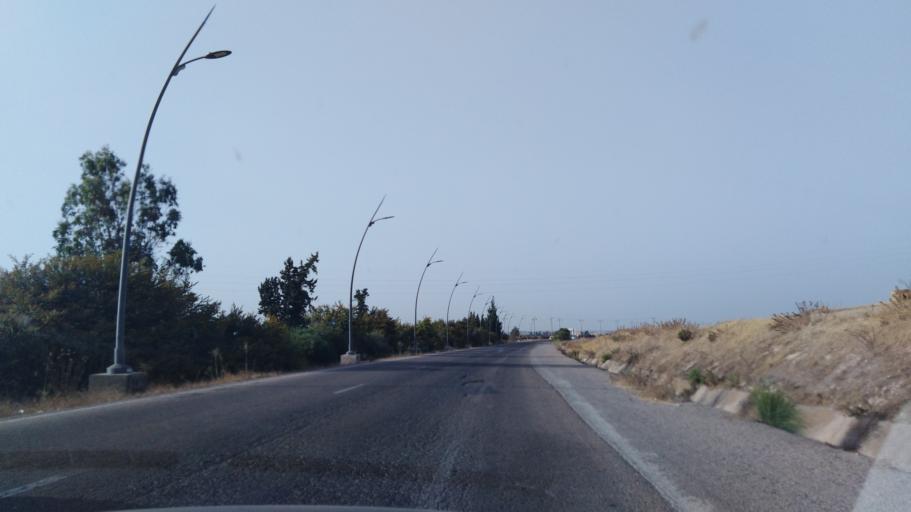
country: MA
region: Chaouia-Ouardigha
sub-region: Settat Province
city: Settat
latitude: 33.0607
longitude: -7.6247
